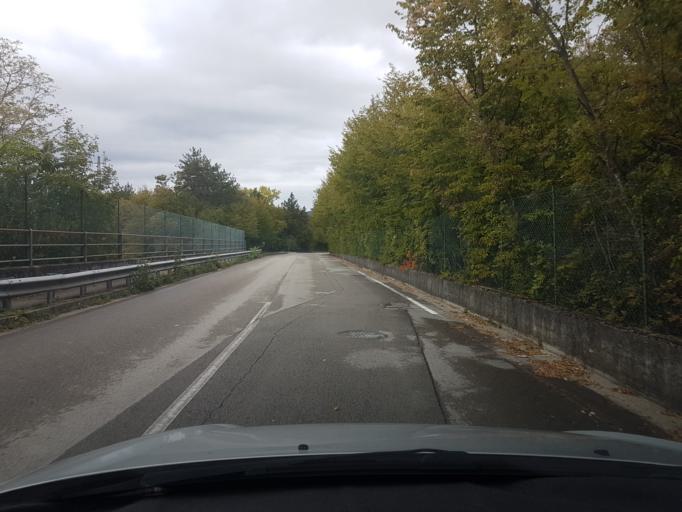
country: IT
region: Friuli Venezia Giulia
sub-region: Provincia di Trieste
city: Aurisina Cave
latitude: 45.7576
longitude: 13.6511
